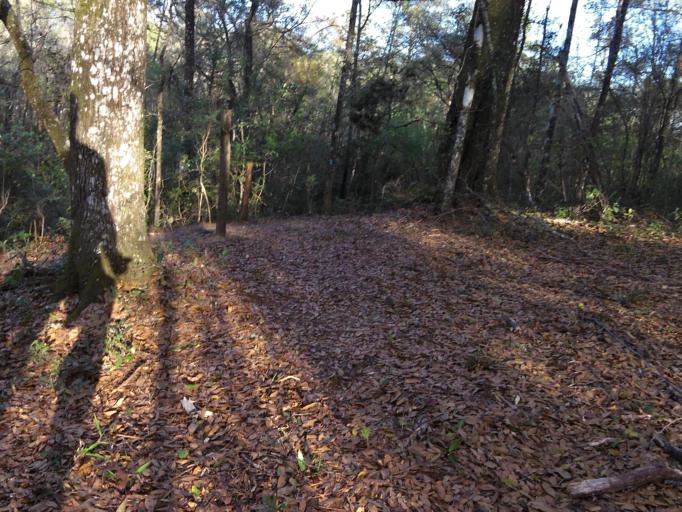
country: US
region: Florida
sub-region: Clay County
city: Middleburg
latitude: 30.1486
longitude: -81.9516
